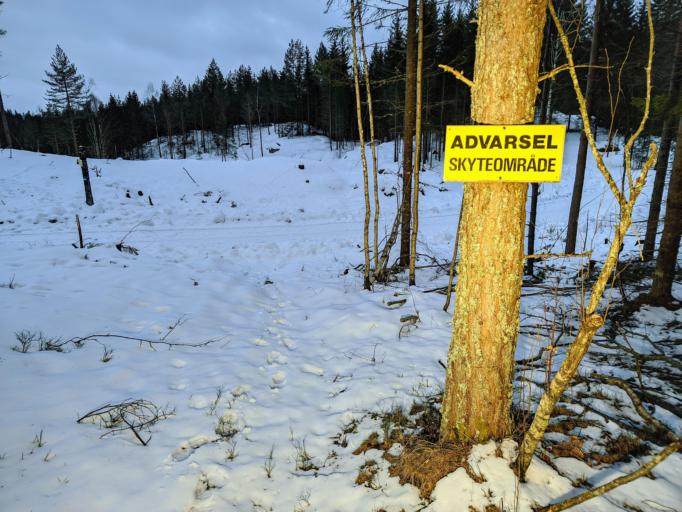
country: NO
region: Akershus
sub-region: Gjerdrum
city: Ask
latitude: 60.0548
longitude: 11.0139
